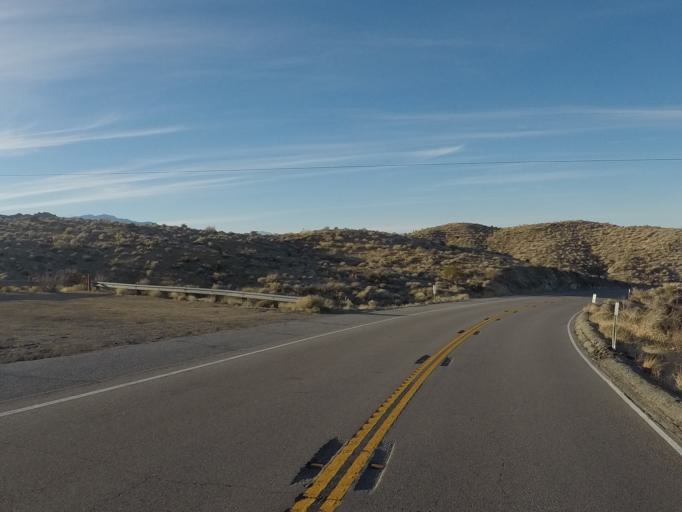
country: US
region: California
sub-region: Riverside County
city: Palm Desert
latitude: 33.6332
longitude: -116.4040
